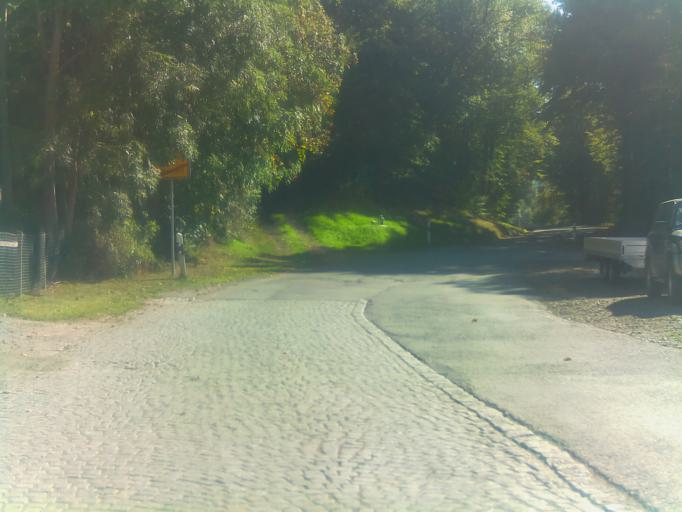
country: DE
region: Thuringia
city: Ottendorf
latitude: 50.8258
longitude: 11.8230
